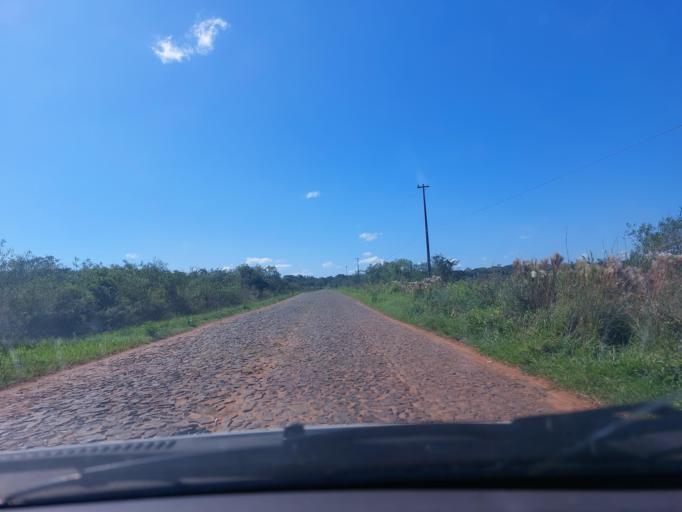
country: PY
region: San Pedro
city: Itacurubi del Rosario
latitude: -24.5881
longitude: -56.6017
